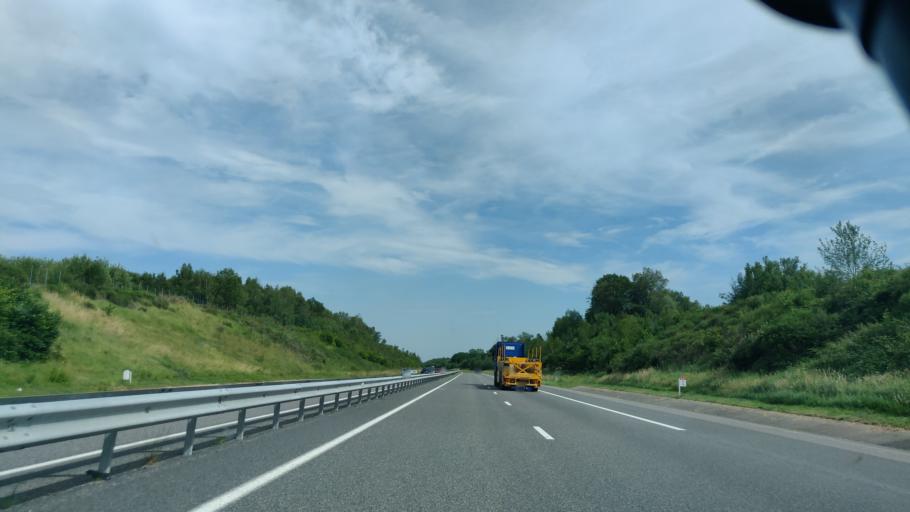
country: FR
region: Lorraine
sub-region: Departement de Meurthe-et-Moselle
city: Baccarat
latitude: 48.5204
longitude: 6.6445
